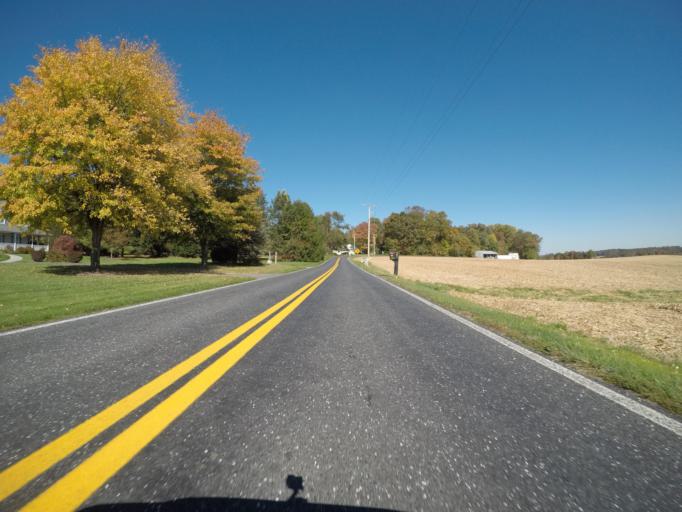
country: US
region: Maryland
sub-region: Carroll County
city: Hampstead
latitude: 39.5586
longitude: -76.8818
